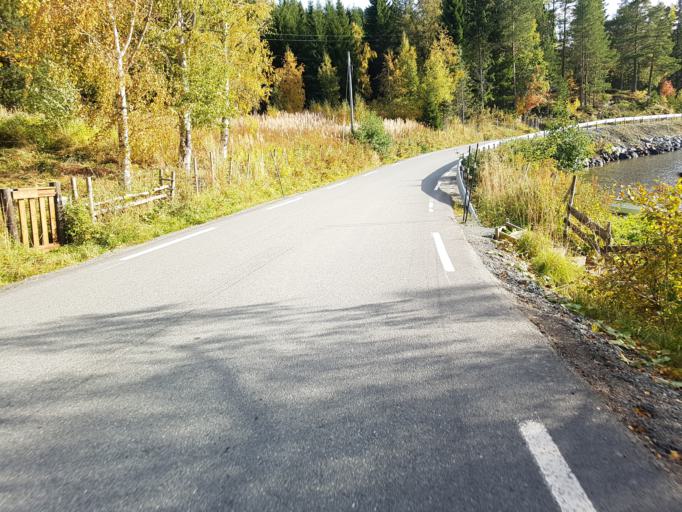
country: NO
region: Sor-Trondelag
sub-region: Malvik
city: Malvik
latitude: 63.3571
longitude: 10.6387
